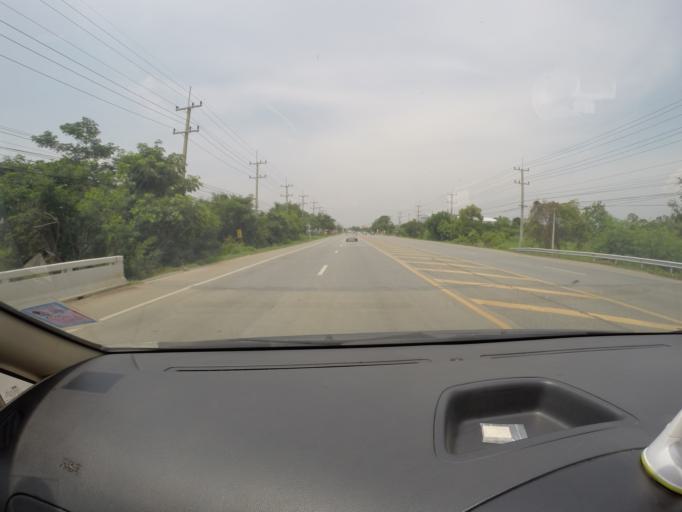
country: TH
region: Chaiyaphum
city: Chaiyaphum
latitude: 15.6932
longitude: 102.0125
